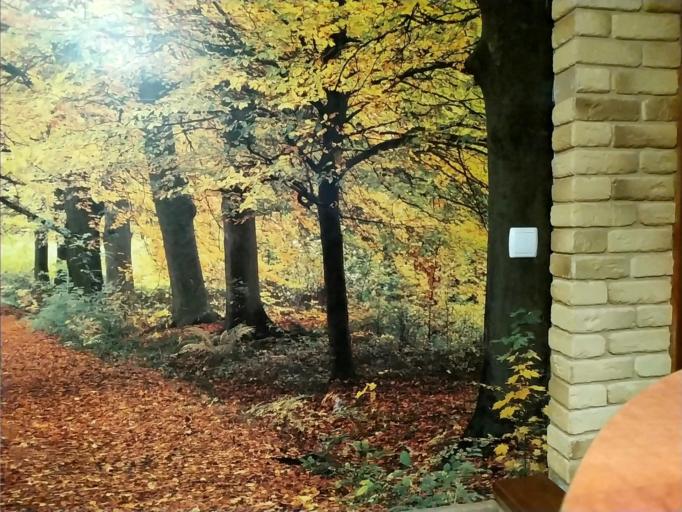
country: BY
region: Minsk
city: Il'ya
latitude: 54.4245
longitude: 27.5305
